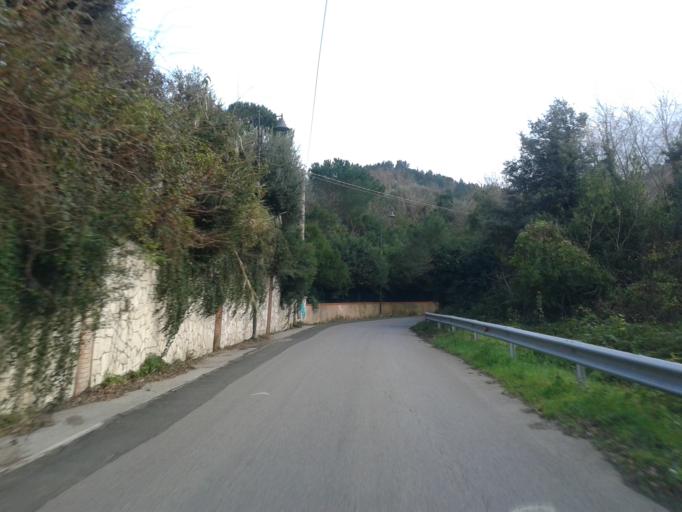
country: IT
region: Tuscany
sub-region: Provincia di Livorno
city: Quercianella
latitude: 43.4961
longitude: 10.3558
